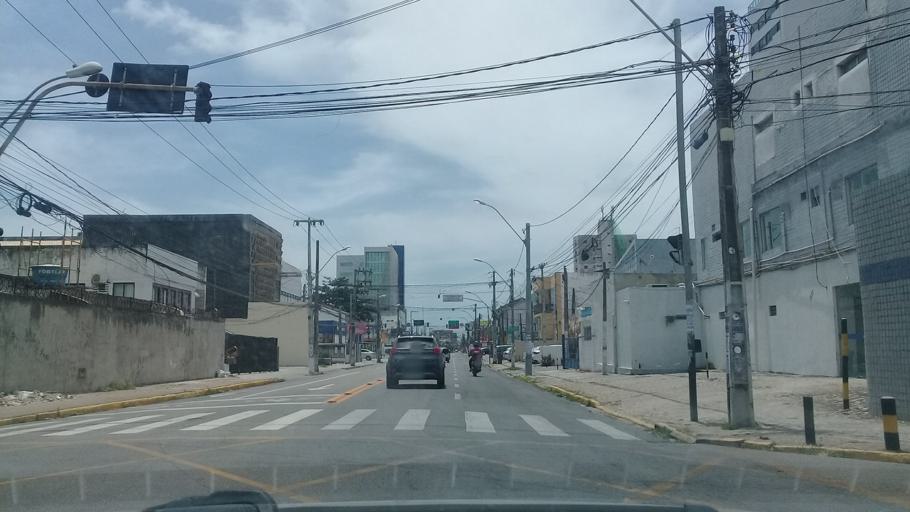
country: BR
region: Pernambuco
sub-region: Olinda
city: Olinda
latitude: -7.9951
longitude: -34.8394
